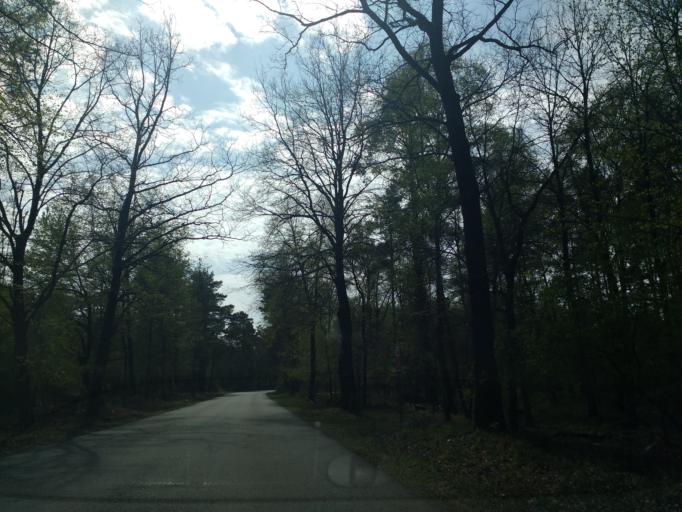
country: DE
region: North Rhine-Westphalia
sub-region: Regierungsbezirk Detmold
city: Hovelhof
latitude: 51.8007
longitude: 8.7221
